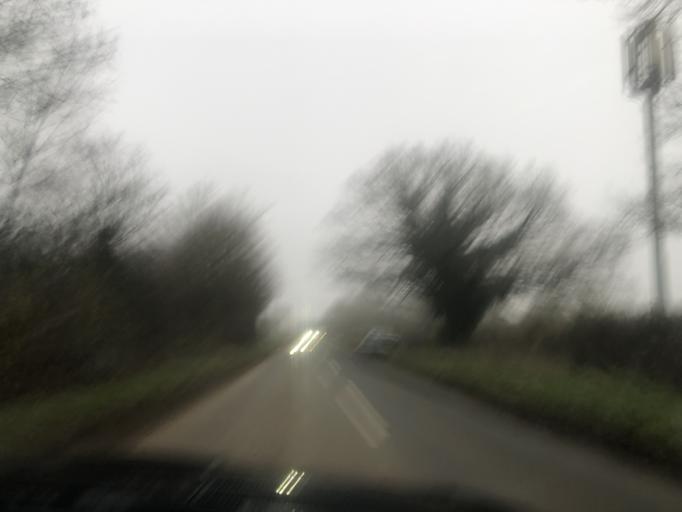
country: GB
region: England
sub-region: Oxfordshire
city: Bicester
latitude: 51.9123
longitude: -1.1715
